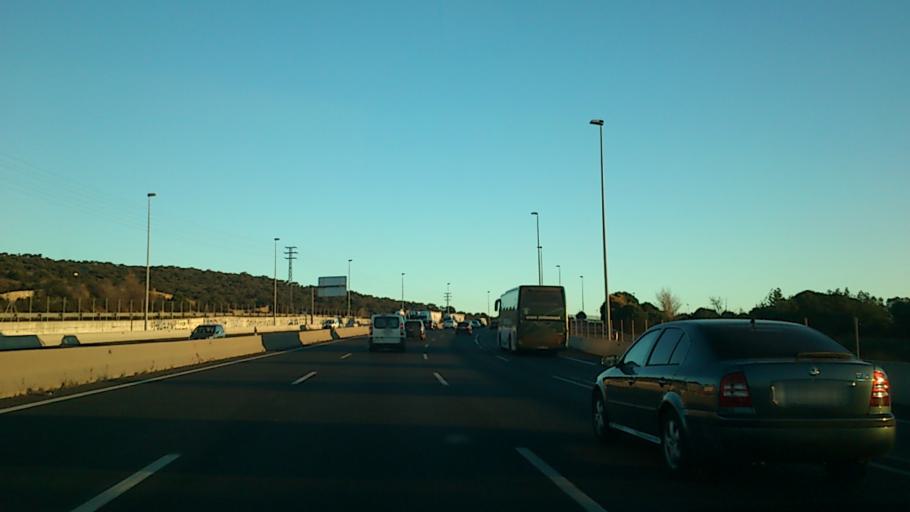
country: ES
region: Madrid
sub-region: Provincia de Madrid
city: Galapagar
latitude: 40.6040
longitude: -3.9663
